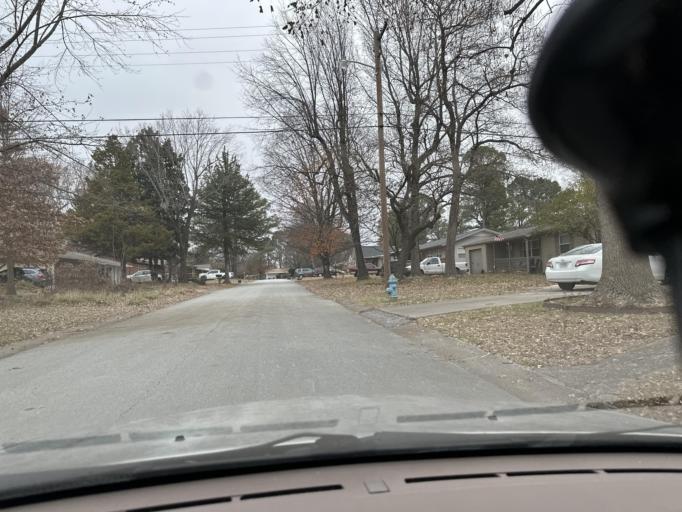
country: US
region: Arkansas
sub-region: Washington County
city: Johnson
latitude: 36.1111
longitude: -94.1423
